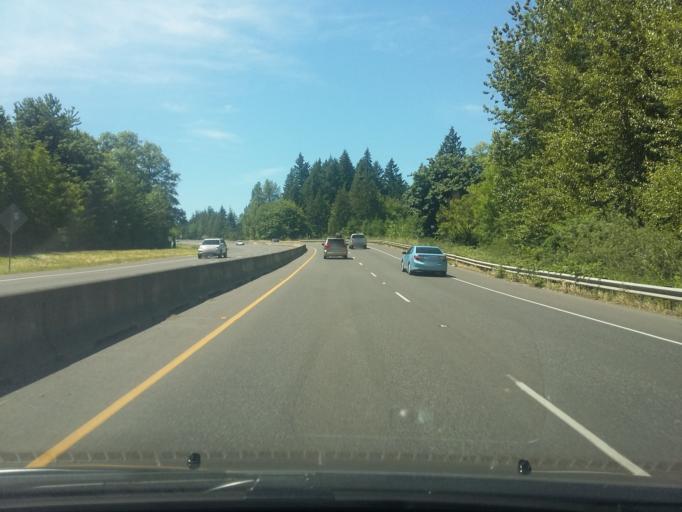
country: US
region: Washington
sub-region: Clark County
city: Five Corners
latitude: 45.6833
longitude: -122.5854
